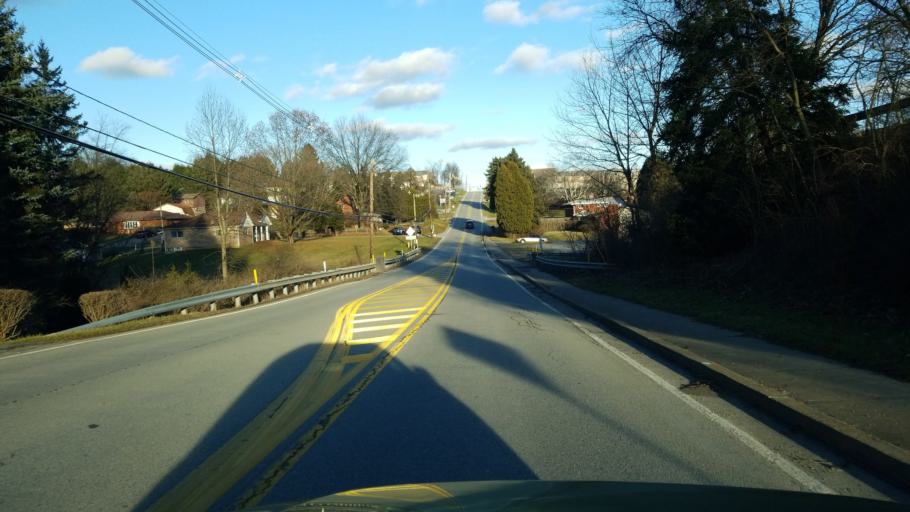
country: US
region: Pennsylvania
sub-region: Indiana County
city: Indiana
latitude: 40.6109
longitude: -79.1849
